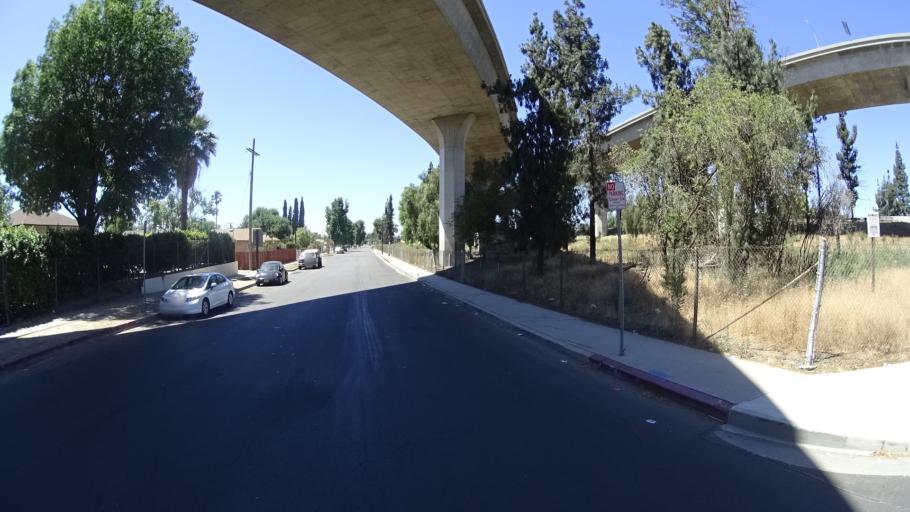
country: US
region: California
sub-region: Los Angeles County
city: San Fernando
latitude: 34.2644
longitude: -118.4711
